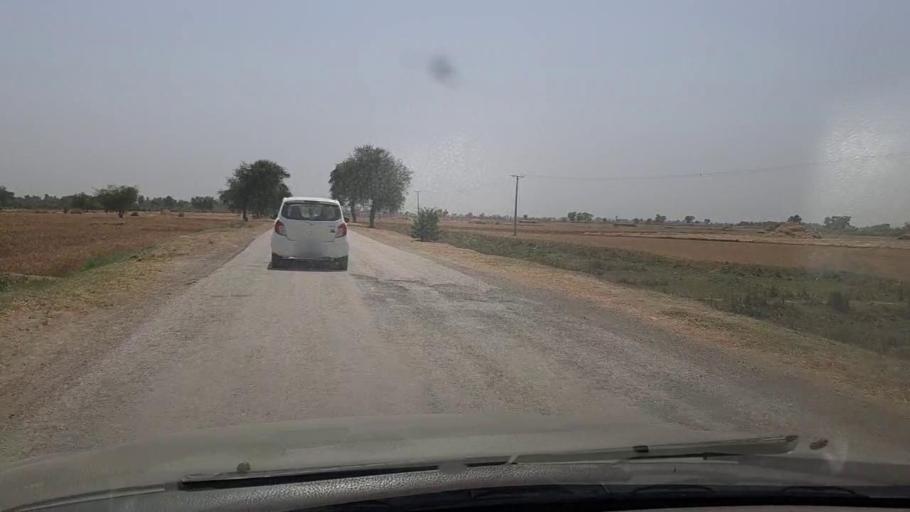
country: PK
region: Sindh
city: Miro Khan
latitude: 27.7216
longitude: 68.0692
